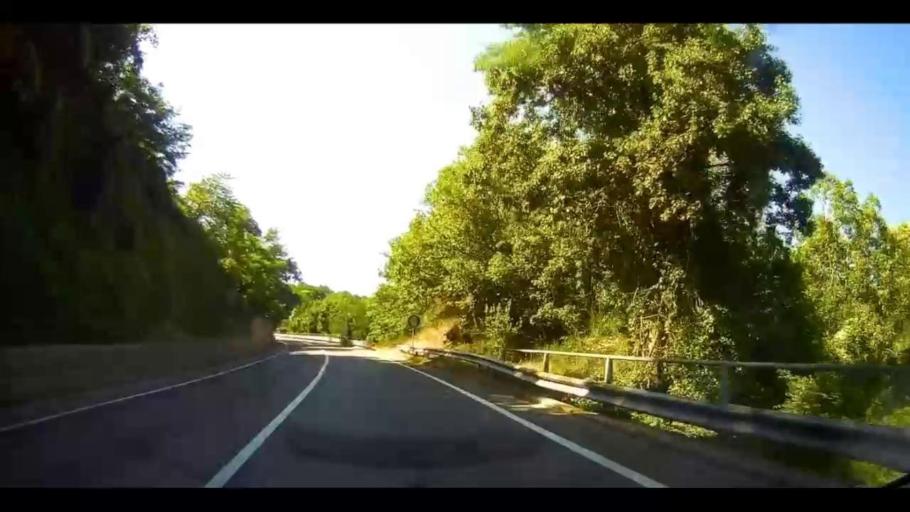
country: IT
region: Calabria
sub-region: Provincia di Cosenza
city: Spezzano Piccolo
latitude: 39.2977
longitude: 16.3552
